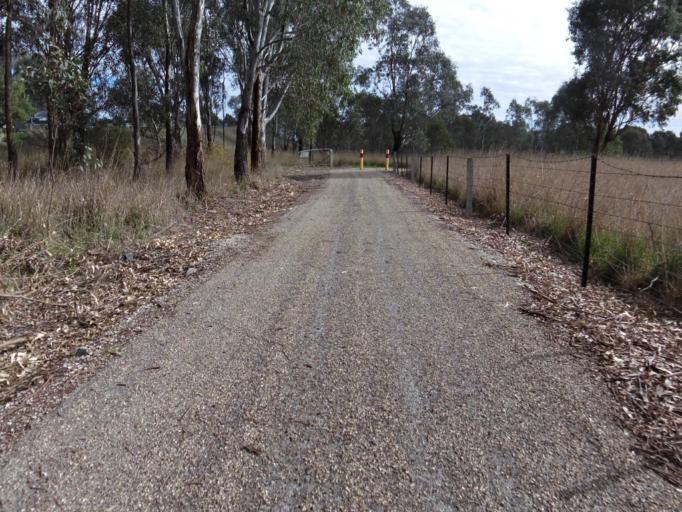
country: AU
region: Victoria
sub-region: Wangaratta
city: Wangaratta
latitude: -36.3949
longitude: 146.3420
